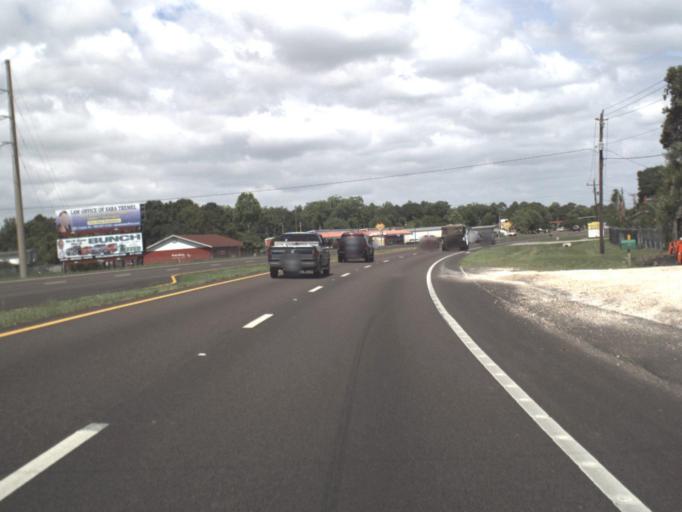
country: US
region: Florida
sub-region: Nassau County
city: Fernandina Beach
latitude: 30.6163
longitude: -81.5087
